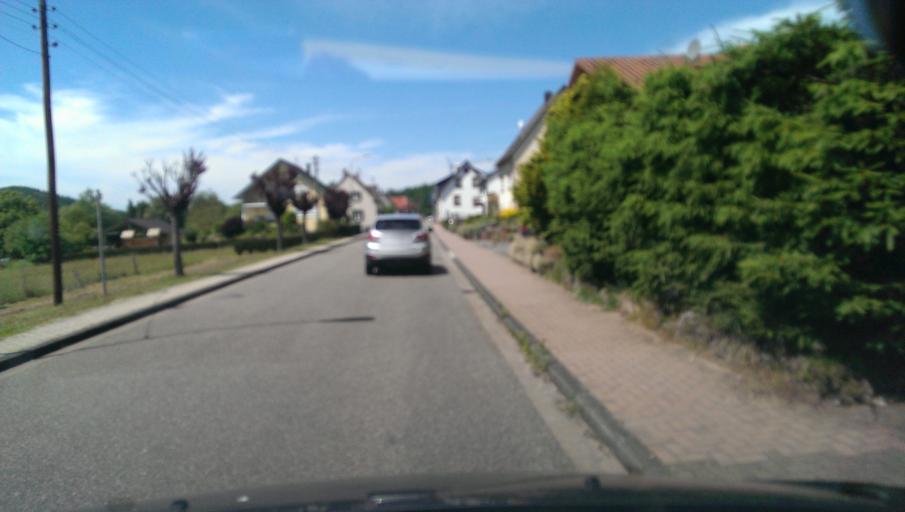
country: DE
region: Rheinland-Pfalz
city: Fischbach
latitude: 49.0877
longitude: 7.7079
